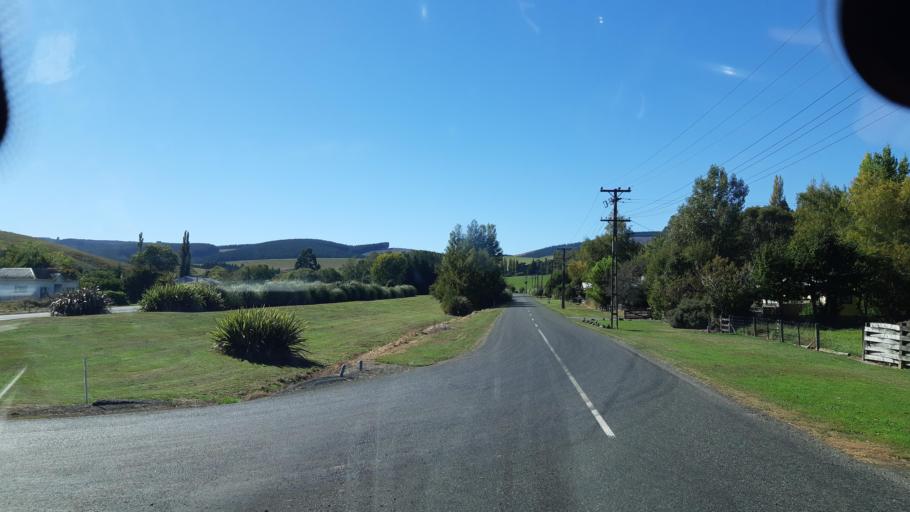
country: NZ
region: Southland
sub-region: Southland District
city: Winton
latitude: -45.8989
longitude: 168.3700
